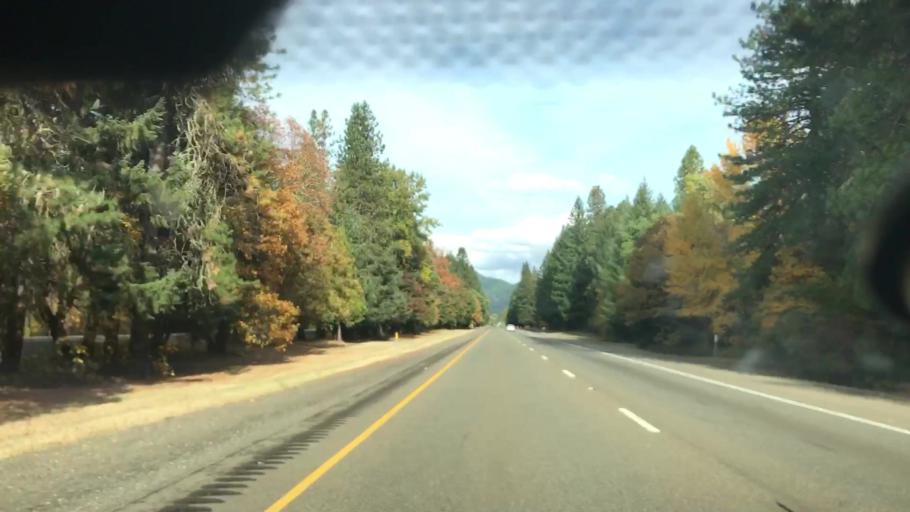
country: US
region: Oregon
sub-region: Douglas County
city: Canyonville
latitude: 42.7526
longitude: -123.3592
